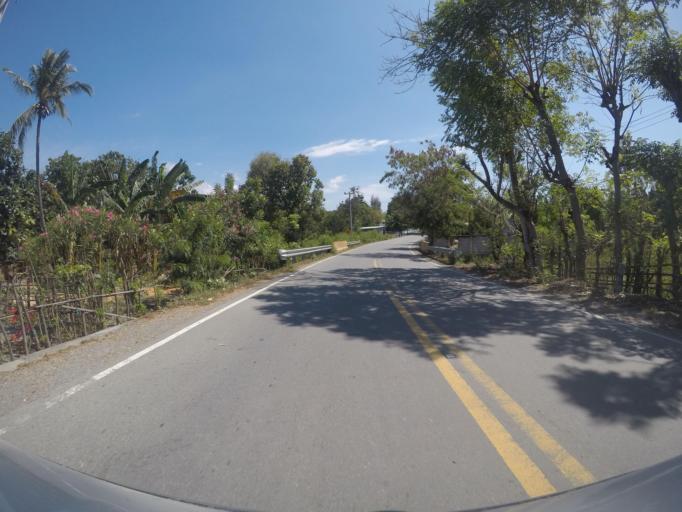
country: TL
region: Liquica
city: Liquica
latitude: -8.5888
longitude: 125.3481
